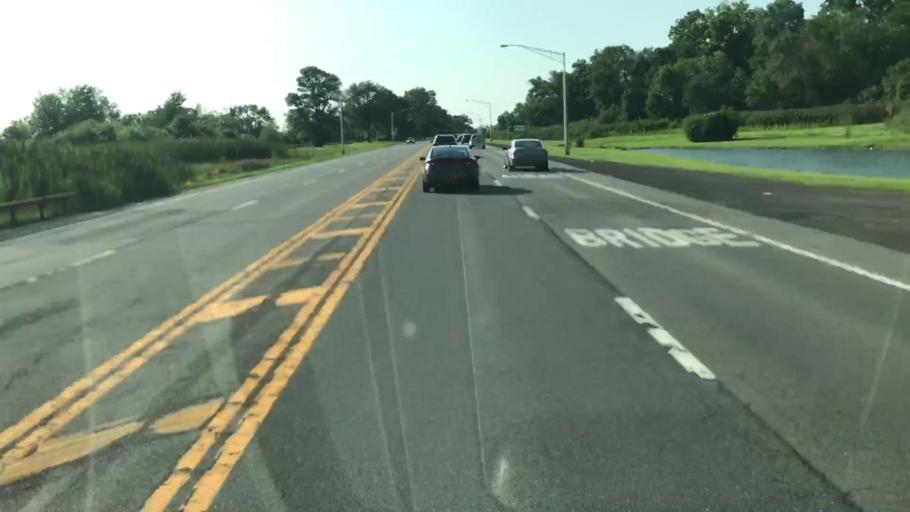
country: US
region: New York
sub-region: Onondaga County
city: Galeville
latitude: 43.0812
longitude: -76.1825
